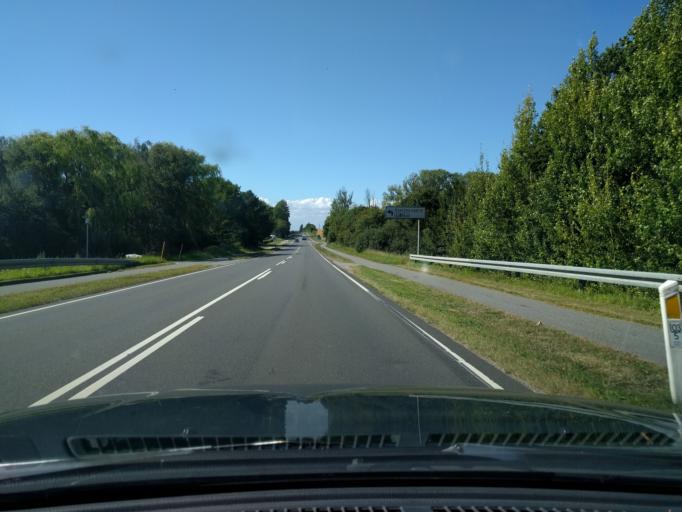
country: DK
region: Zealand
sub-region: Slagelse Kommune
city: Korsor
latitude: 55.3233
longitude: 11.1903
